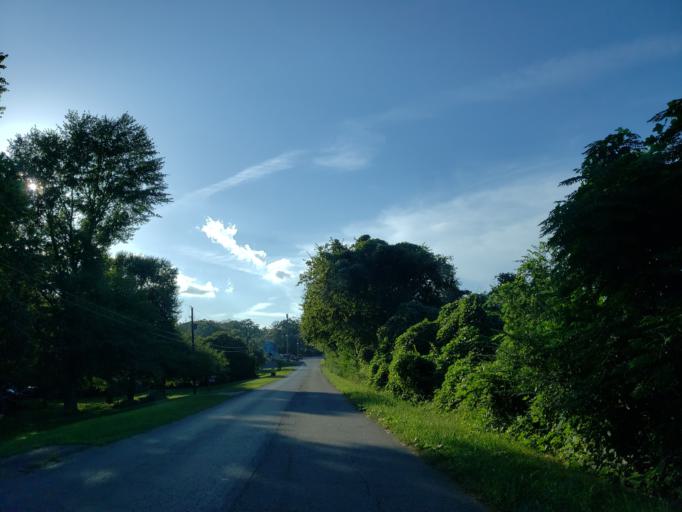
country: US
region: Georgia
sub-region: Bartow County
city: Cartersville
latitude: 34.2108
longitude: -84.8316
